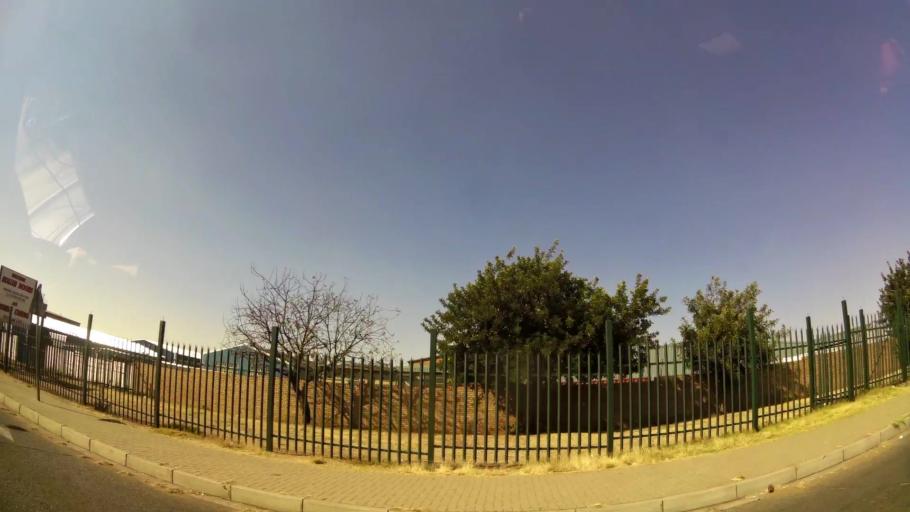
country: ZA
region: Gauteng
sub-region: City of Johannesburg Metropolitan Municipality
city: Johannesburg
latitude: -26.1811
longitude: 27.9642
